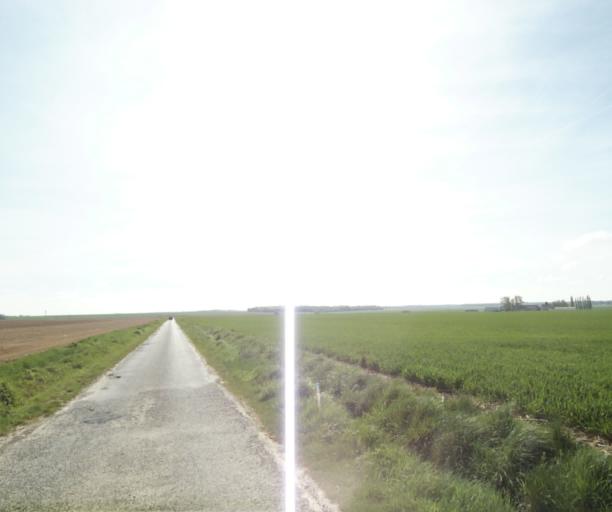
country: FR
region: Ile-de-France
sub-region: Departement de Seine-et-Marne
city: Nangis
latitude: 48.5525
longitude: 3.0279
